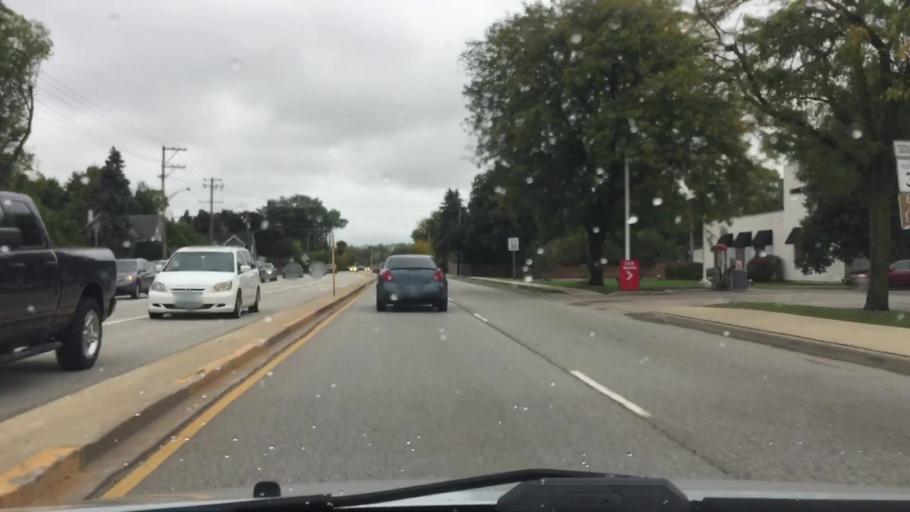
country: US
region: Illinois
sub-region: Kane County
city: West Dundee
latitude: 42.0978
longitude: -88.2872
